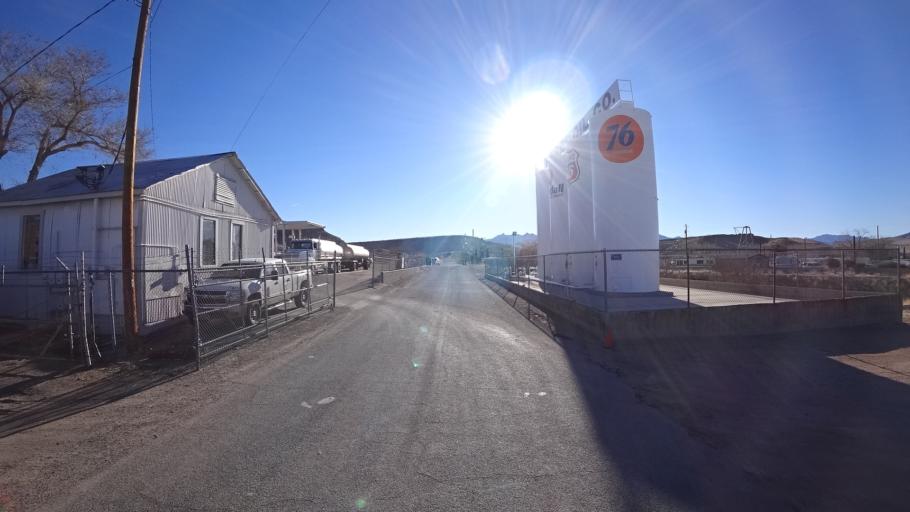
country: US
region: Arizona
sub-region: Mohave County
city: Kingman
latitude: 35.1853
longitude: -114.0415
